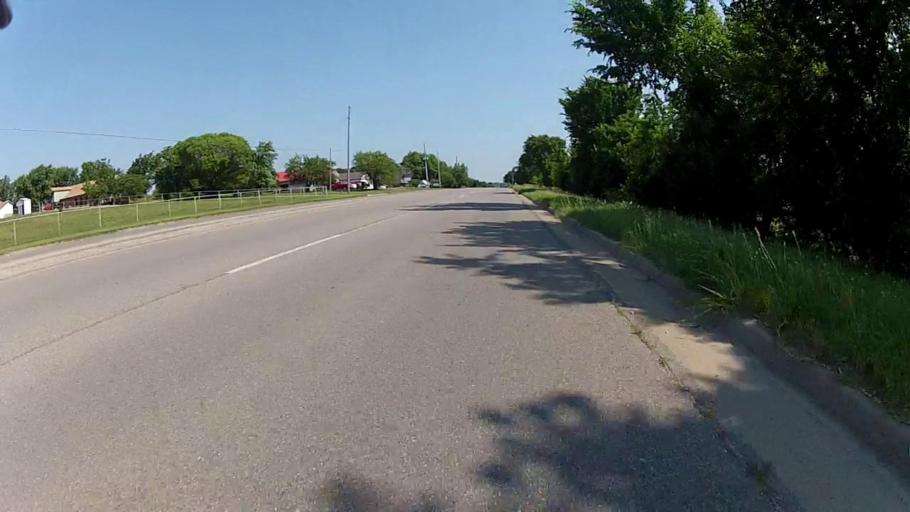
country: US
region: Kansas
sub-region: Montgomery County
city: Independence
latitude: 37.2021
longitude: -95.7106
